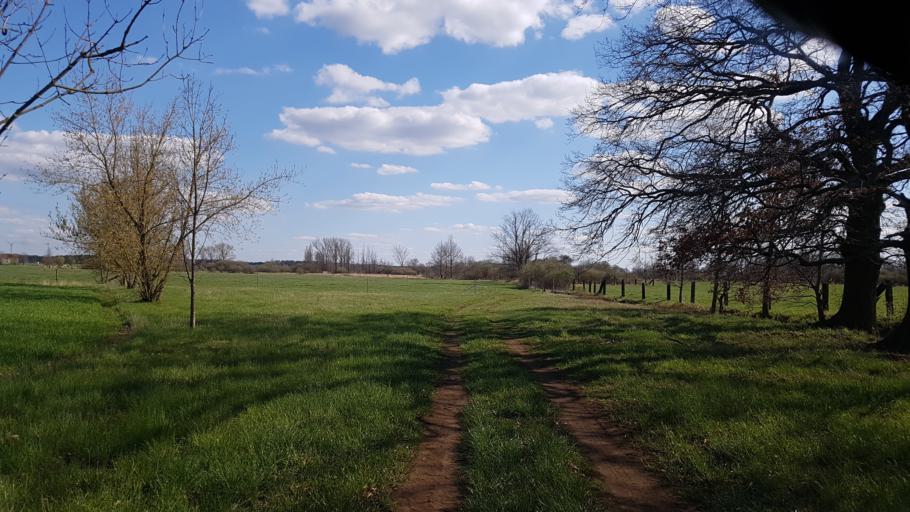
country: DE
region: Brandenburg
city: Falkenberg
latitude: 51.5079
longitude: 13.2698
